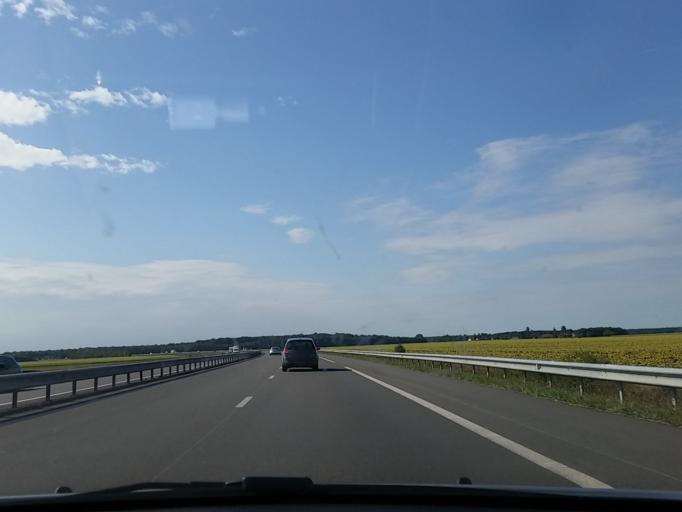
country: FR
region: Centre
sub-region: Departement du Cher
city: Levet
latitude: 46.9528
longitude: 2.4169
